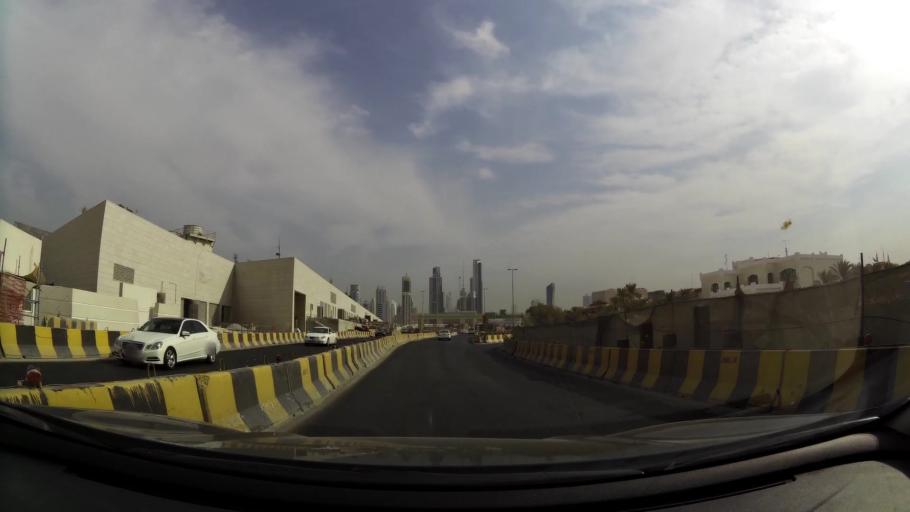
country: KW
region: Al Asimah
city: Ash Shamiyah
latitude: 29.3568
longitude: 47.9537
